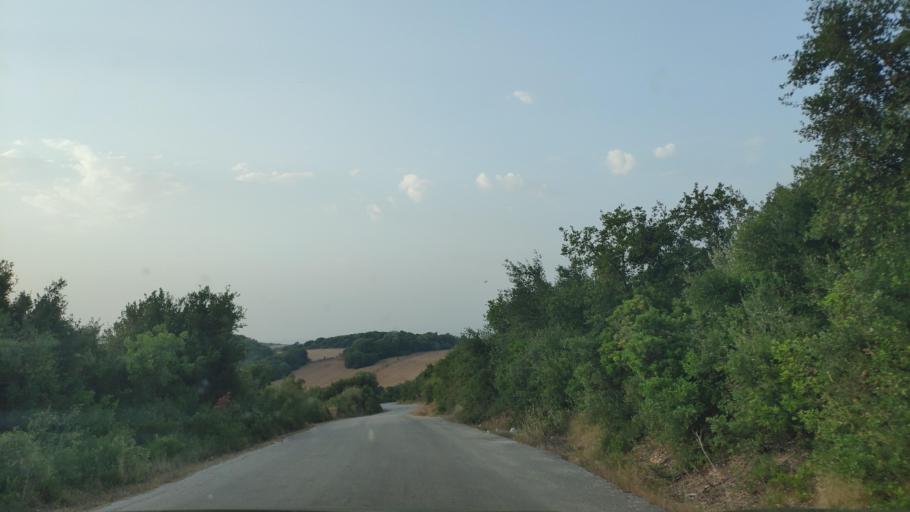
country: GR
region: West Greece
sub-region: Nomos Aitolias kai Akarnanias
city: Monastirakion
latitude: 38.9206
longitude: 20.9801
